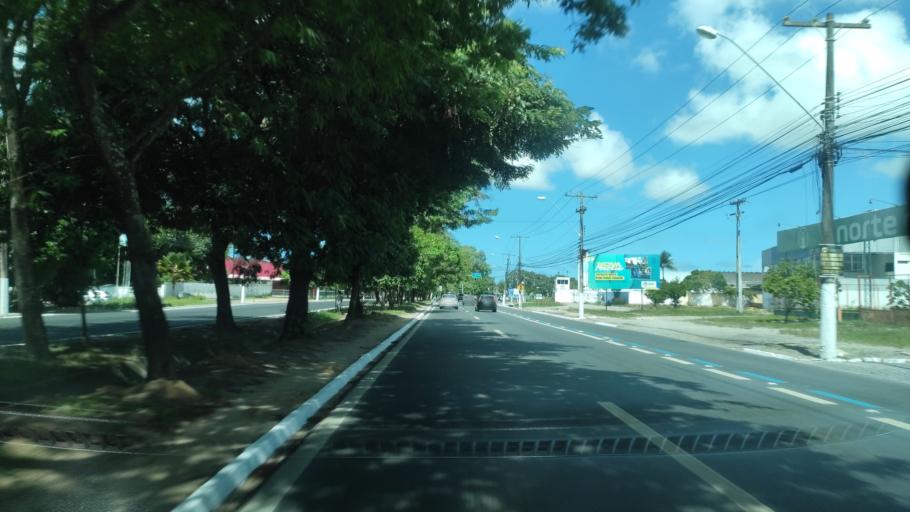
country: BR
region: Alagoas
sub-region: Maceio
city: Maceio
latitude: -9.5939
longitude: -35.7539
